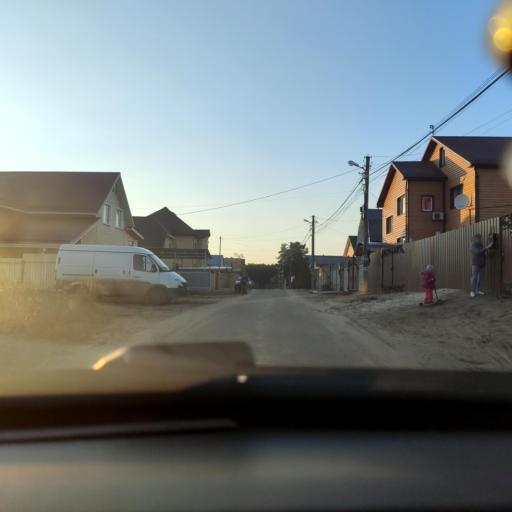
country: RU
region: Voronezj
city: Shilovo
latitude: 51.5767
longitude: 39.0453
